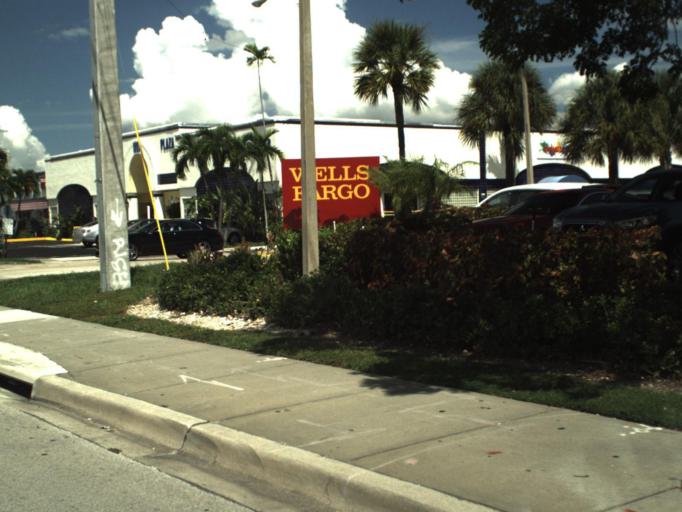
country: US
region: Florida
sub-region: Broward County
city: Hallandale Beach
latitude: 25.9859
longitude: -80.1360
